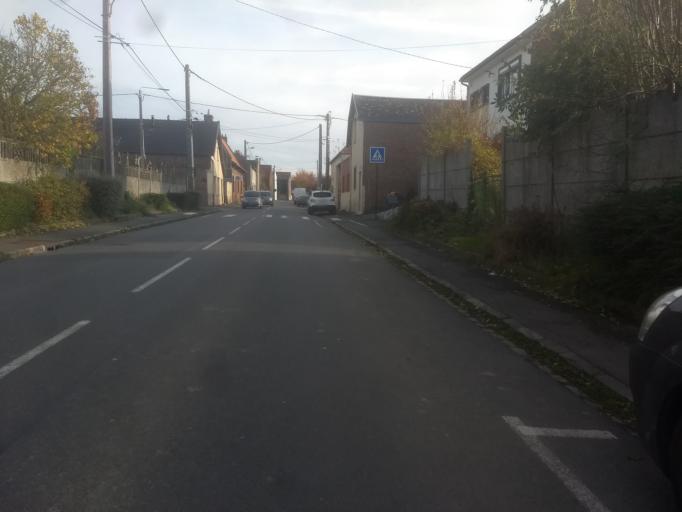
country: FR
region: Nord-Pas-de-Calais
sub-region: Departement du Pas-de-Calais
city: Agny
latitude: 50.2594
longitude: 2.7616
